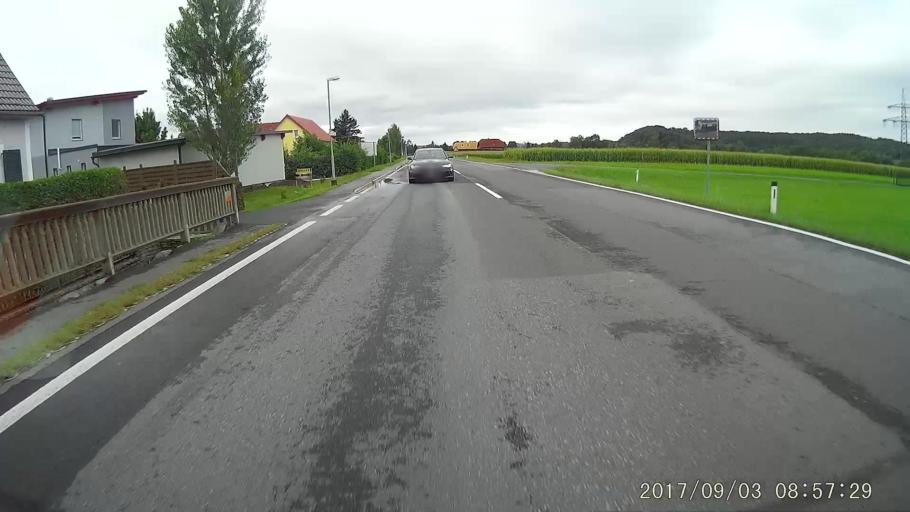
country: AT
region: Styria
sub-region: Politischer Bezirk Suedoststeiermark
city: Merkendorf
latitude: 46.8621
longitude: 15.9028
